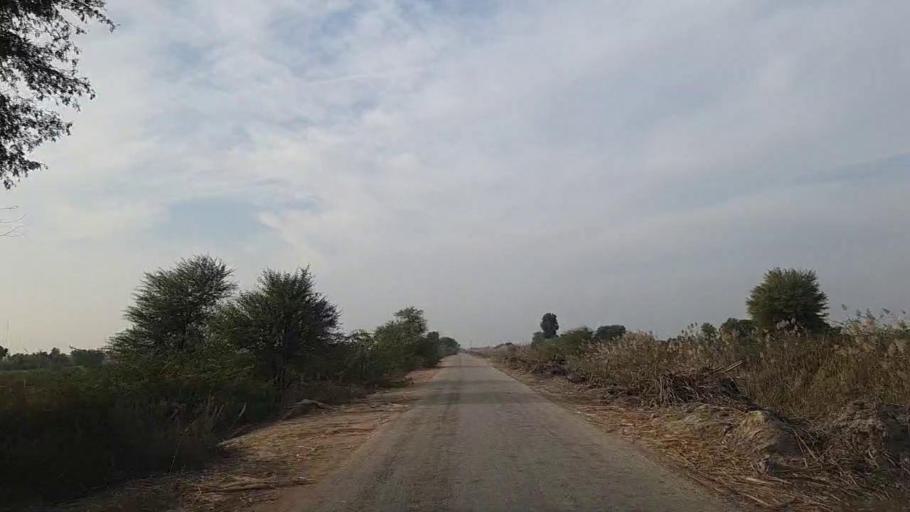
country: PK
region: Sindh
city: Daur
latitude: 26.4967
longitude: 68.4504
